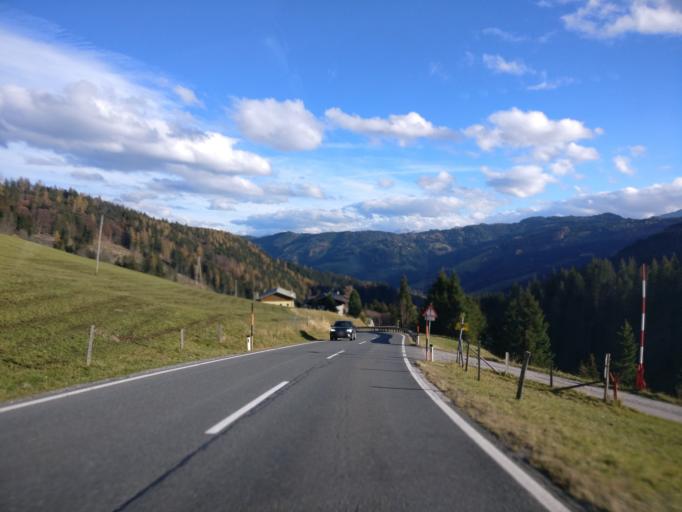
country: AT
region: Salzburg
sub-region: Politischer Bezirk Sankt Johann im Pongau
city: Muhlbach am Hochkonig
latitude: 47.3933
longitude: 13.0893
